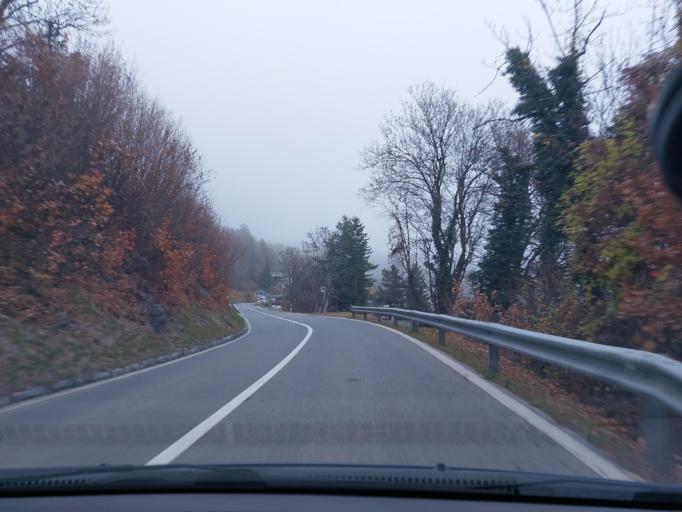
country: CH
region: Valais
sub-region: Sierre District
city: Veyras
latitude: 46.3128
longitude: 7.5161
